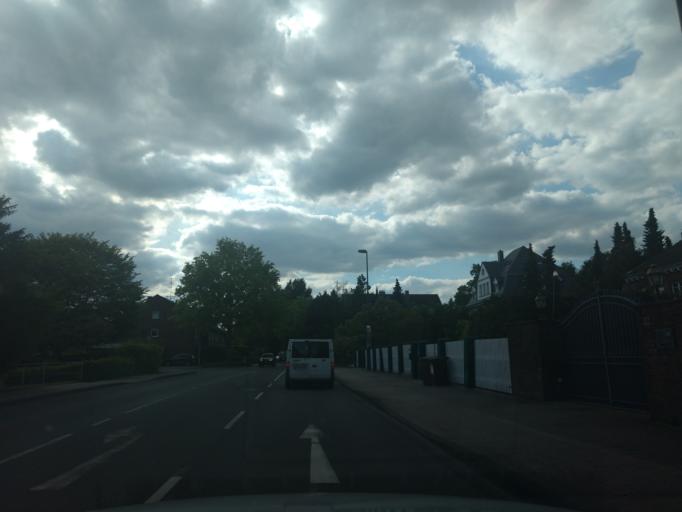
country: DE
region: North Rhine-Westphalia
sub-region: Regierungsbezirk Dusseldorf
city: Meerbusch
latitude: 51.2539
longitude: 6.7039
